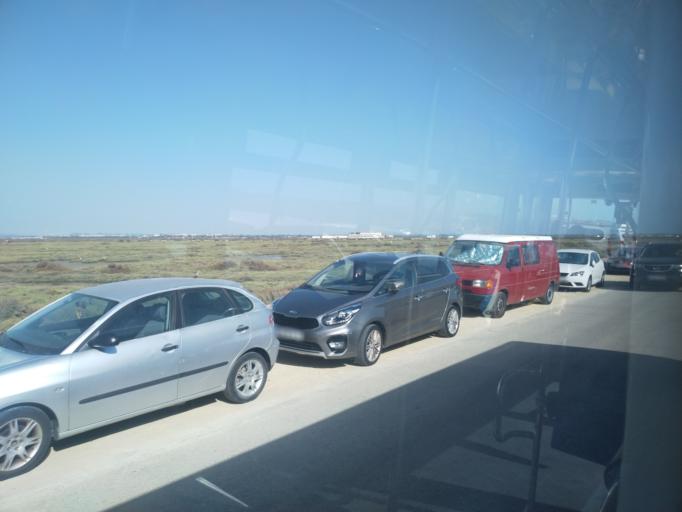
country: ES
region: Andalusia
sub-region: Provincia de Cadiz
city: San Fernando
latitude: 36.4248
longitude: -6.2272
